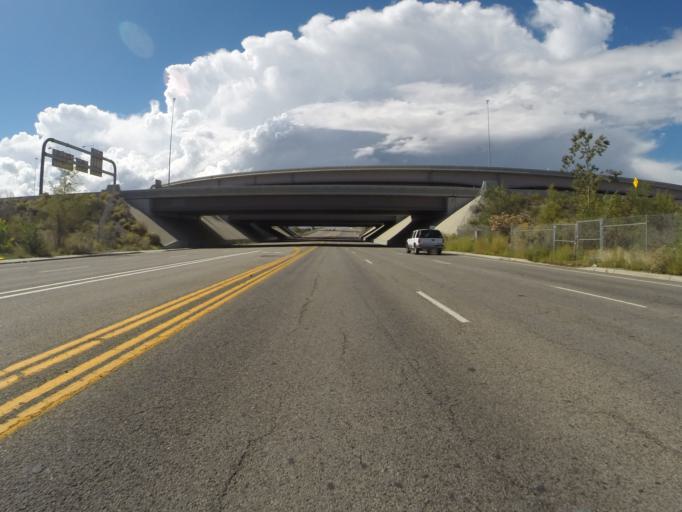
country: US
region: Utah
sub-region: Salt Lake County
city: South Salt Lake
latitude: 40.7254
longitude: -111.9029
